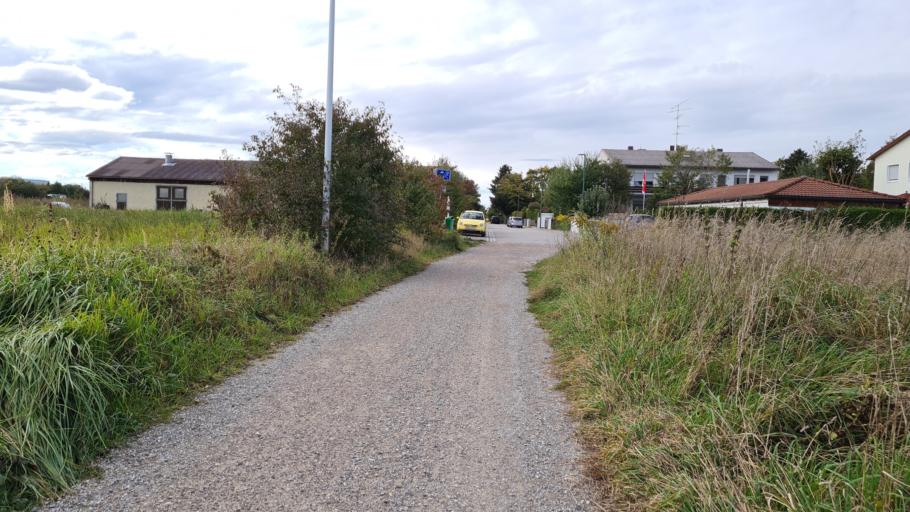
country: DE
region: Bavaria
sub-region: Upper Bavaria
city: Grafelfing
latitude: 48.1102
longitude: 11.4428
